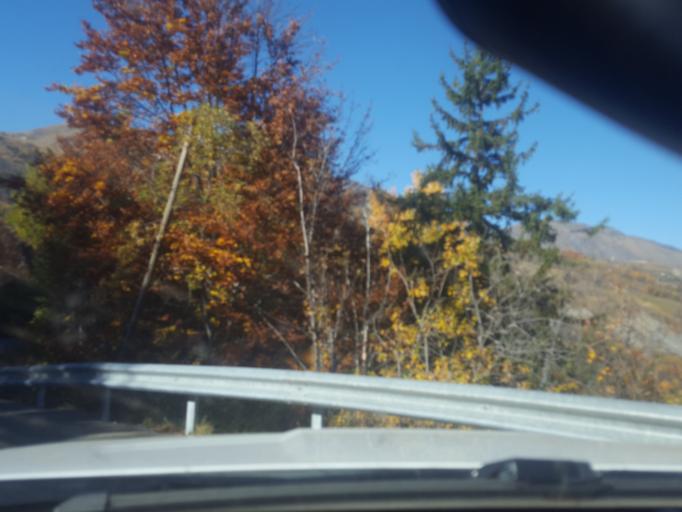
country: FR
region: Rhone-Alpes
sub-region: Departement de la Savoie
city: Saint-Jean-de-Maurienne
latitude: 45.2394
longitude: 6.2815
